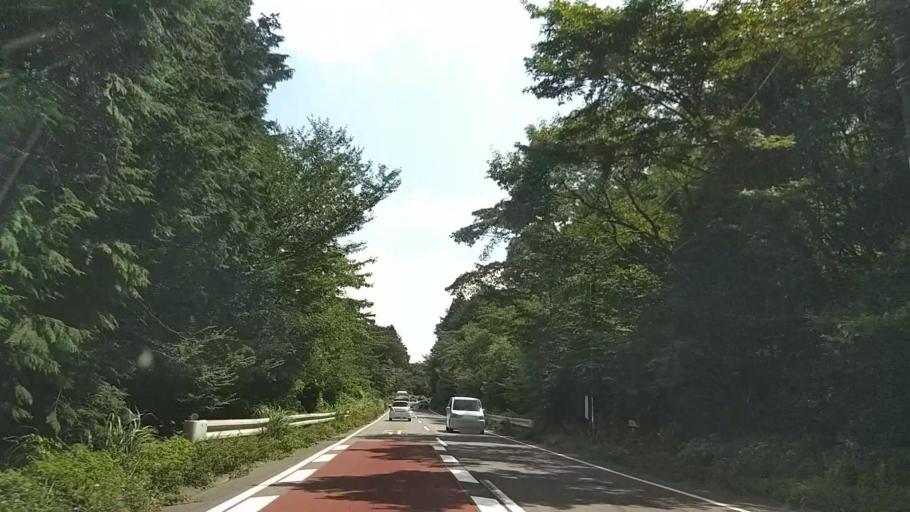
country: JP
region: Shizuoka
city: Fujinomiya
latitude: 35.3493
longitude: 138.5847
